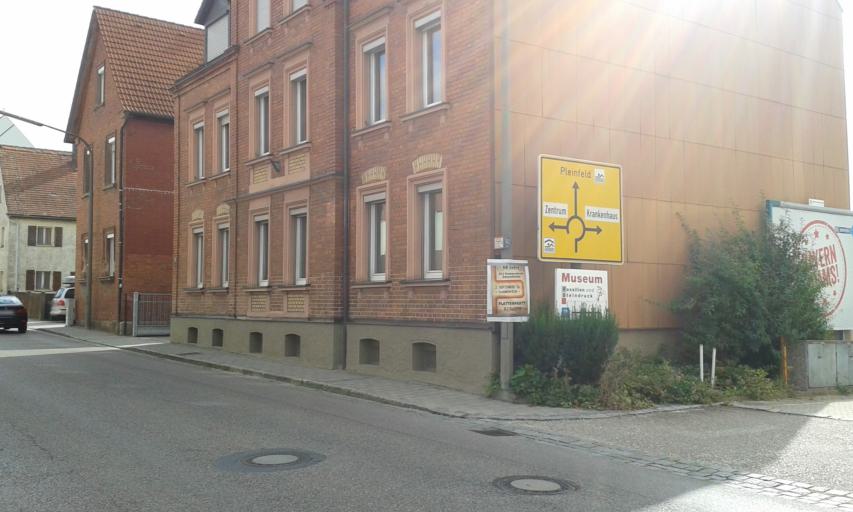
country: DE
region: Bavaria
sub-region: Regierungsbezirk Mittelfranken
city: Gunzenhausen
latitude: 49.1120
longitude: 10.7564
